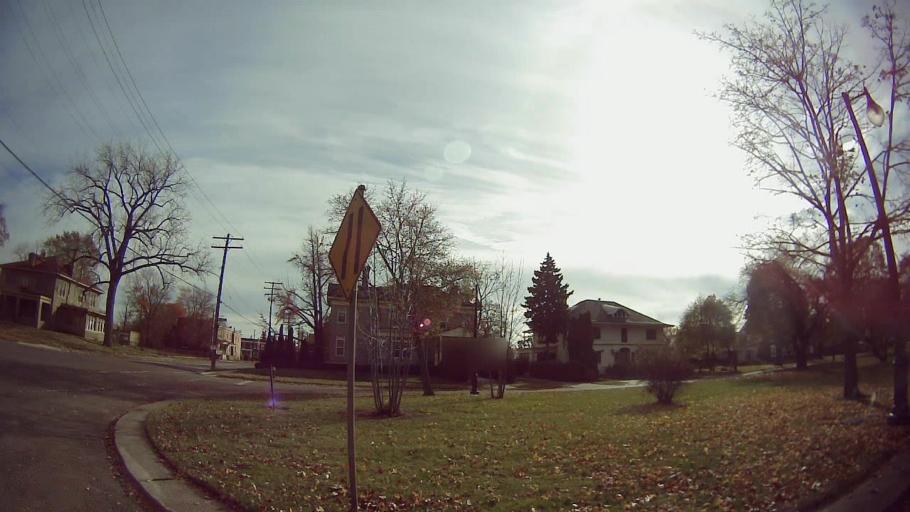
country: US
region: Michigan
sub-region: Wayne County
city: Highland Park
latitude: 42.3886
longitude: -83.0783
